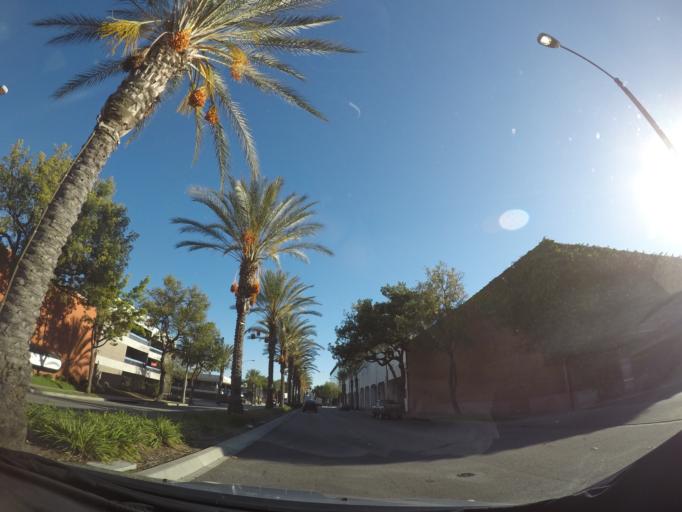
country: US
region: California
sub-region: Los Angeles County
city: South Pasadena
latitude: 34.1299
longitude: -118.1474
